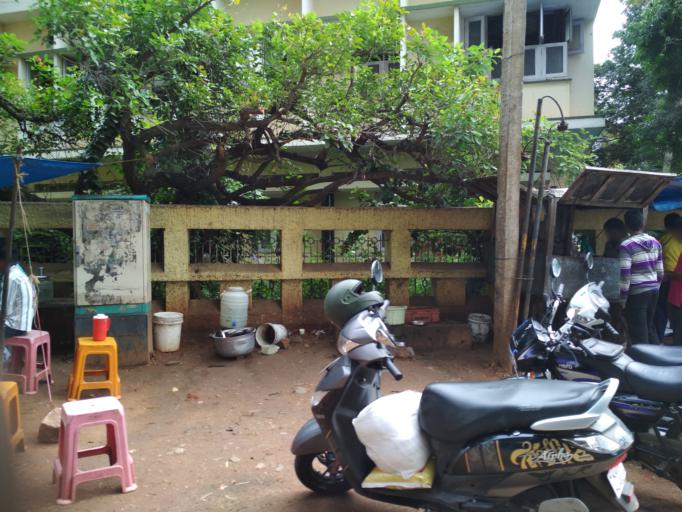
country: IN
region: Karnataka
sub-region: Mysore
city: Mysore
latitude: 12.3228
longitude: 76.6295
